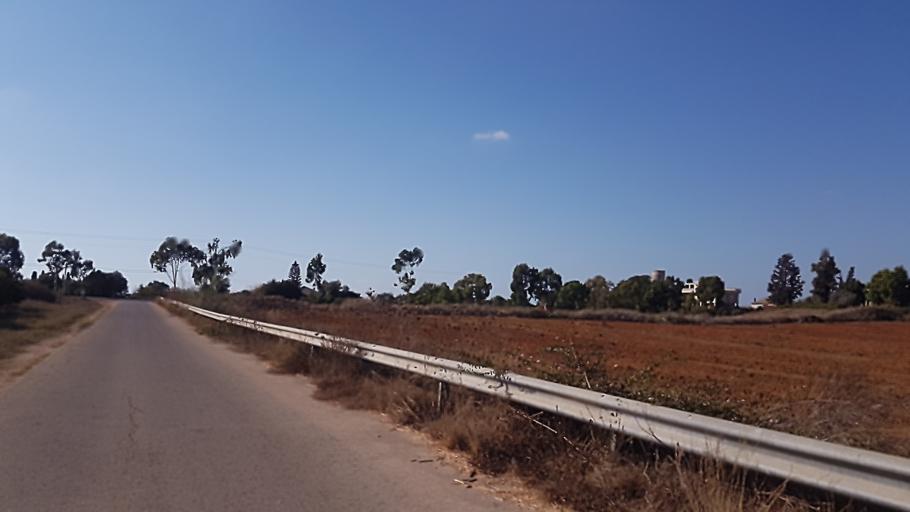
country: IL
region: Central District
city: Kfar Saba
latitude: 32.2020
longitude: 34.9159
